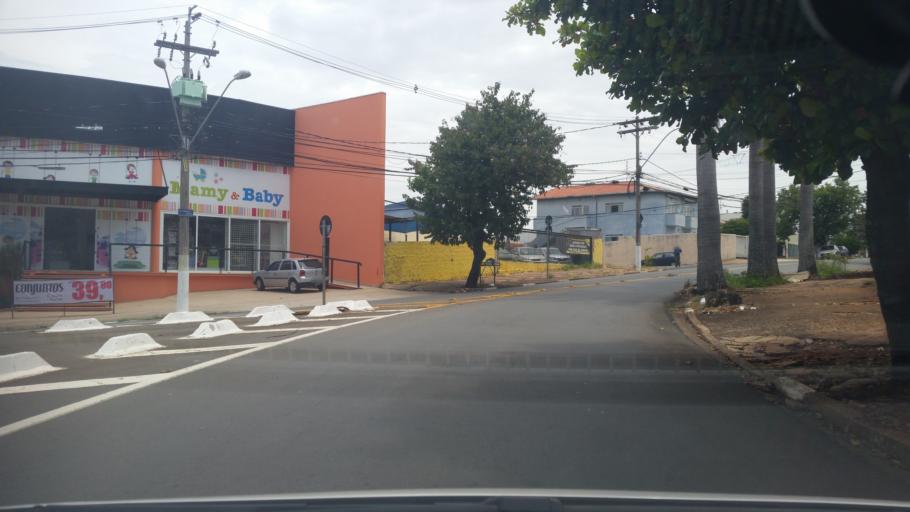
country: BR
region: Sao Paulo
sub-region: Campinas
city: Campinas
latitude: -22.8731
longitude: -47.0629
